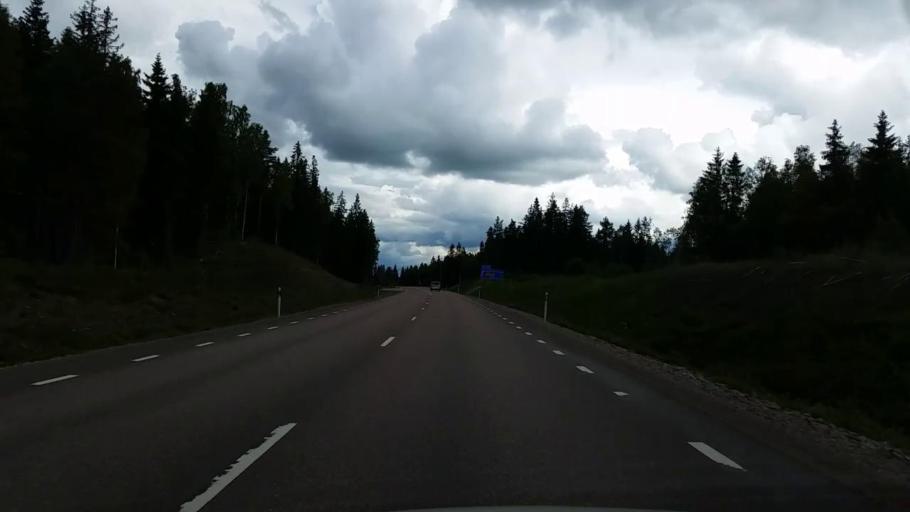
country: SE
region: Dalarna
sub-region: Avesta Kommun
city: Horndal
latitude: 60.4682
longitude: 16.4485
